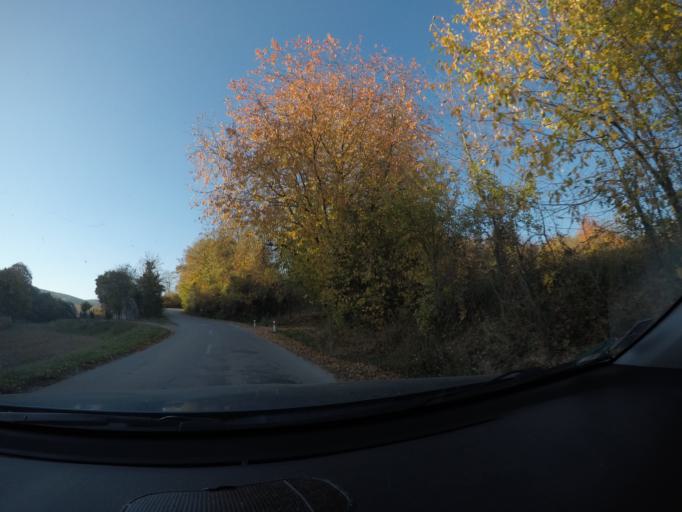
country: SK
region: Nitriansky
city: Nemsova
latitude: 48.9703
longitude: 18.0945
